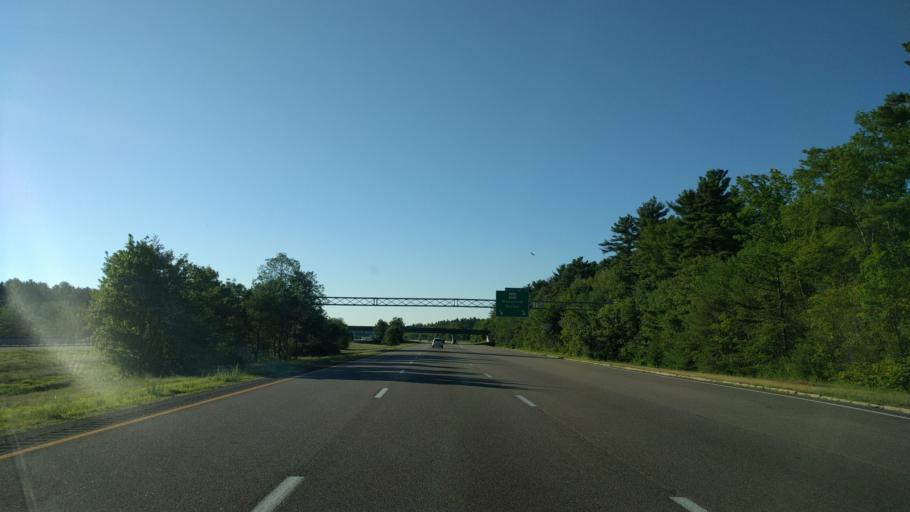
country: US
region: Massachusetts
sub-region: Bristol County
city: Mansfield Center
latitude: 42.0086
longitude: -71.2277
